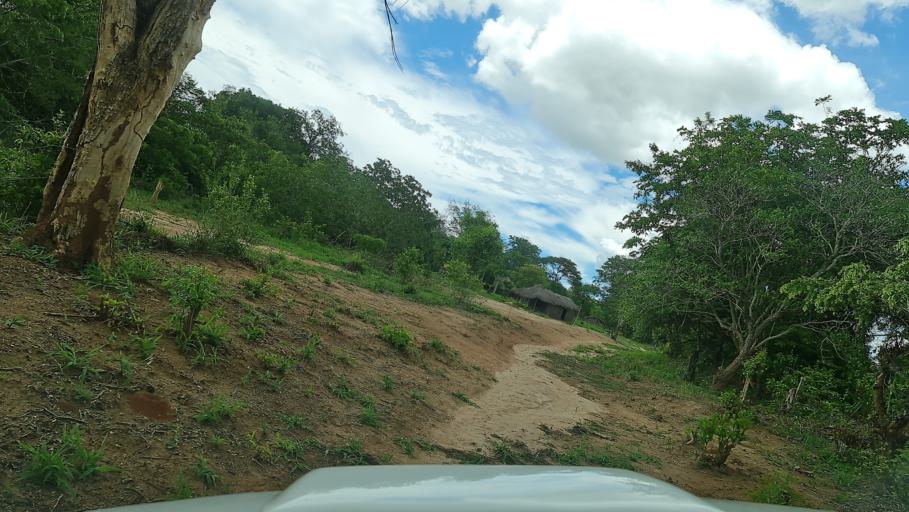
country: MZ
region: Nampula
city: Ilha de Mocambique
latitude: -15.5042
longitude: 40.1867
